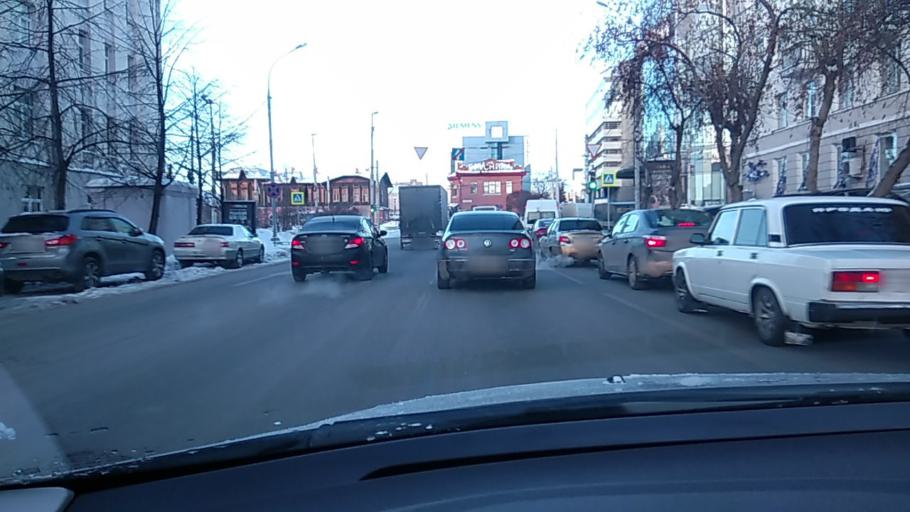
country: RU
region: Sverdlovsk
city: Yekaterinburg
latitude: 56.8349
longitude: 60.6142
